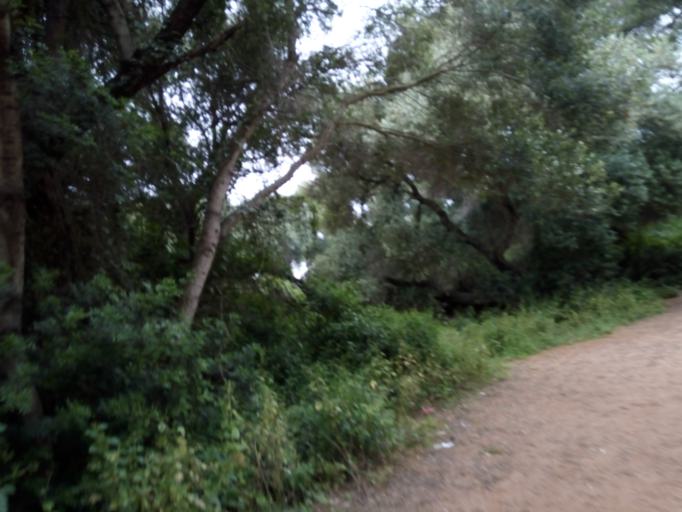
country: DZ
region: Tipaza
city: Tipasa
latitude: 36.5935
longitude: 2.4415
